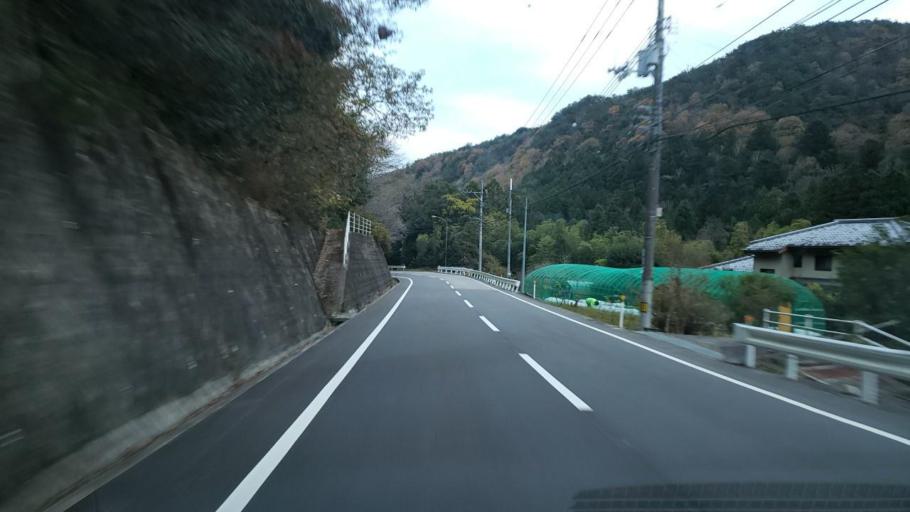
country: JP
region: Tokushima
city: Wakimachi
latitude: 34.1811
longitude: 134.2354
